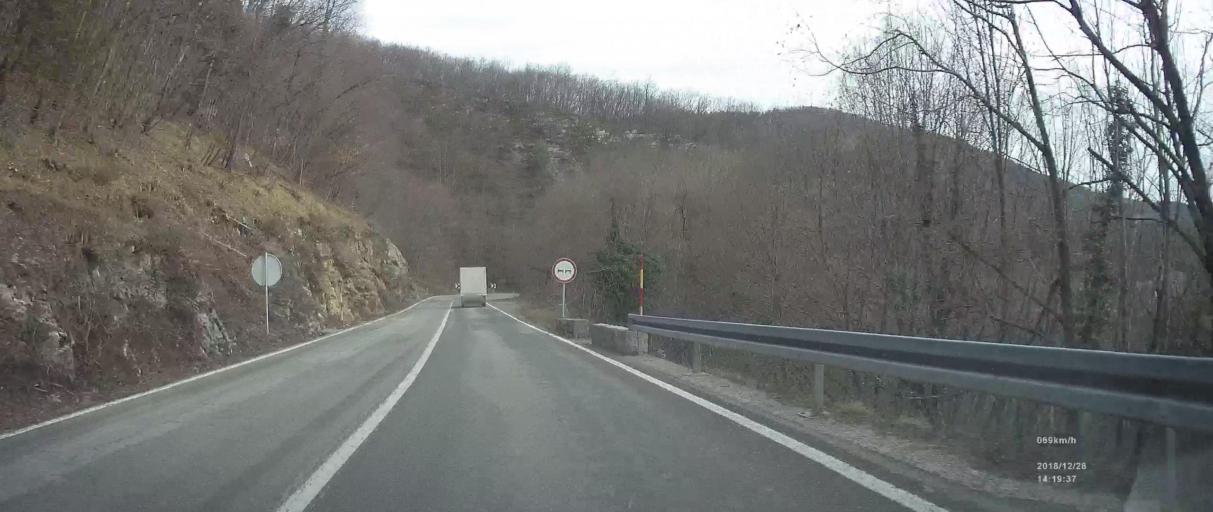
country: HR
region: Primorsko-Goranska
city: Vrbovsko
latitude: 45.4026
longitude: 15.0691
